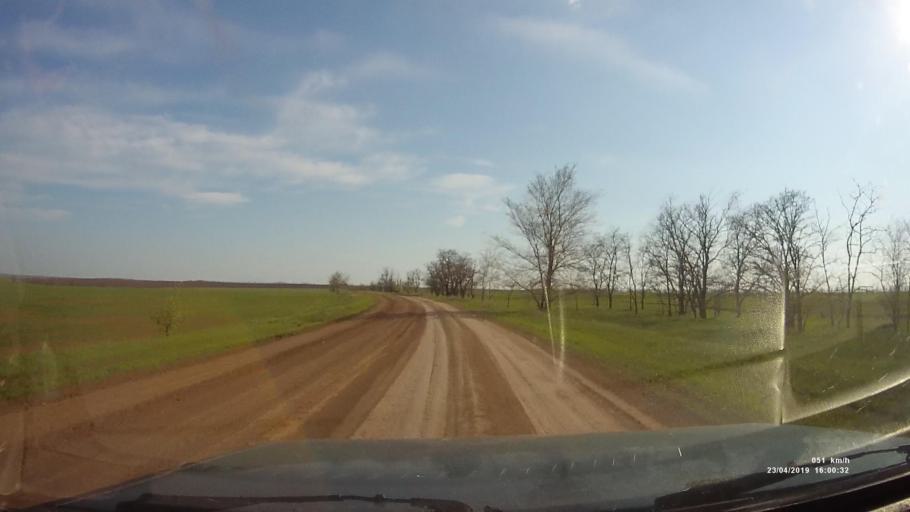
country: RU
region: Rostov
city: Remontnoye
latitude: 46.5089
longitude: 43.1073
